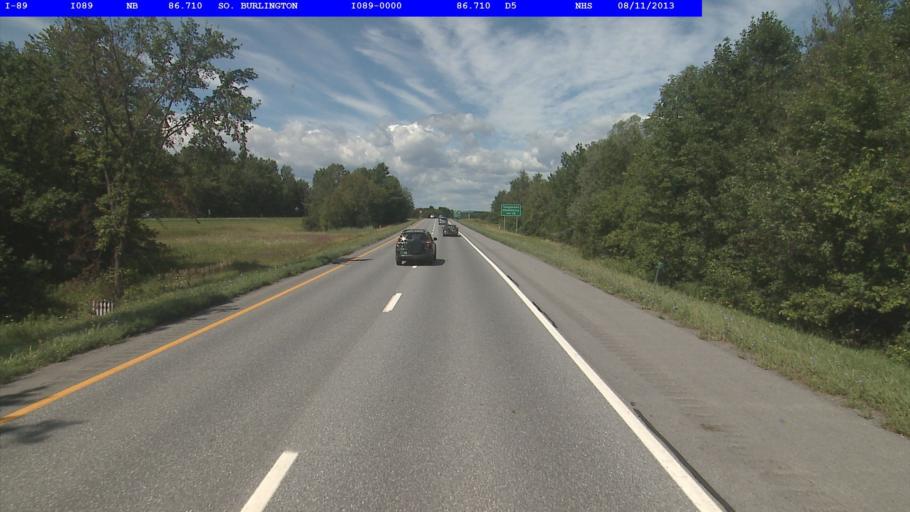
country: US
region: Vermont
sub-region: Chittenden County
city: South Burlington
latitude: 44.4496
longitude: -73.1682
